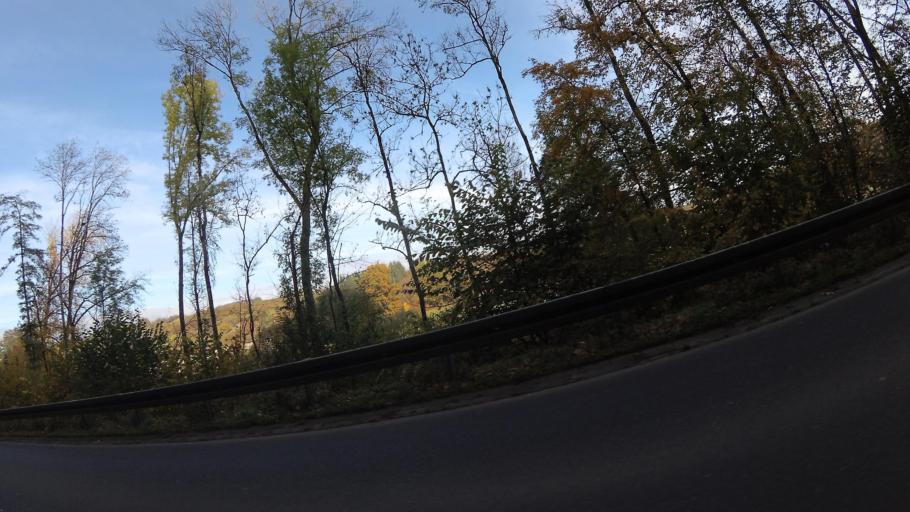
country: DE
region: Baden-Wuerttemberg
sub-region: Regierungsbezirk Stuttgart
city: Mockmuhl
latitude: 49.3027
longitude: 9.3540
